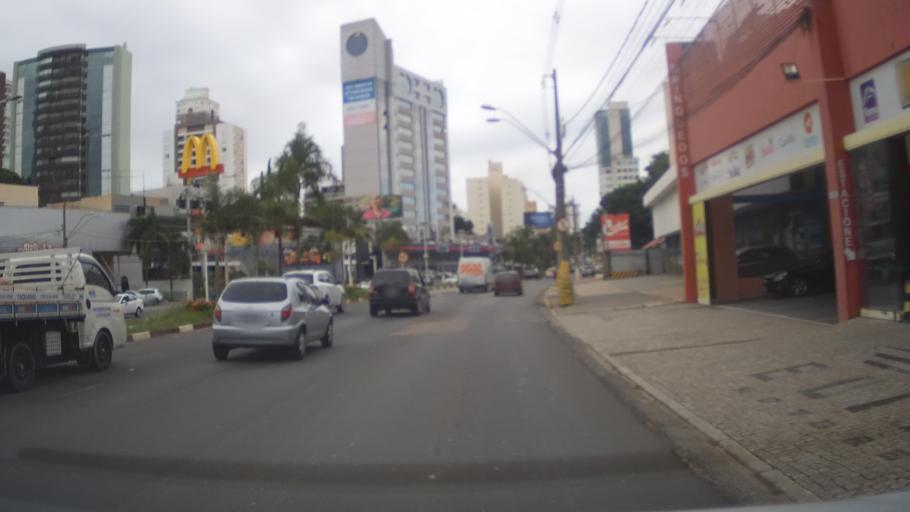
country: BR
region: Sao Paulo
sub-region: Campinas
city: Campinas
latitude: -22.8933
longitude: -47.0473
